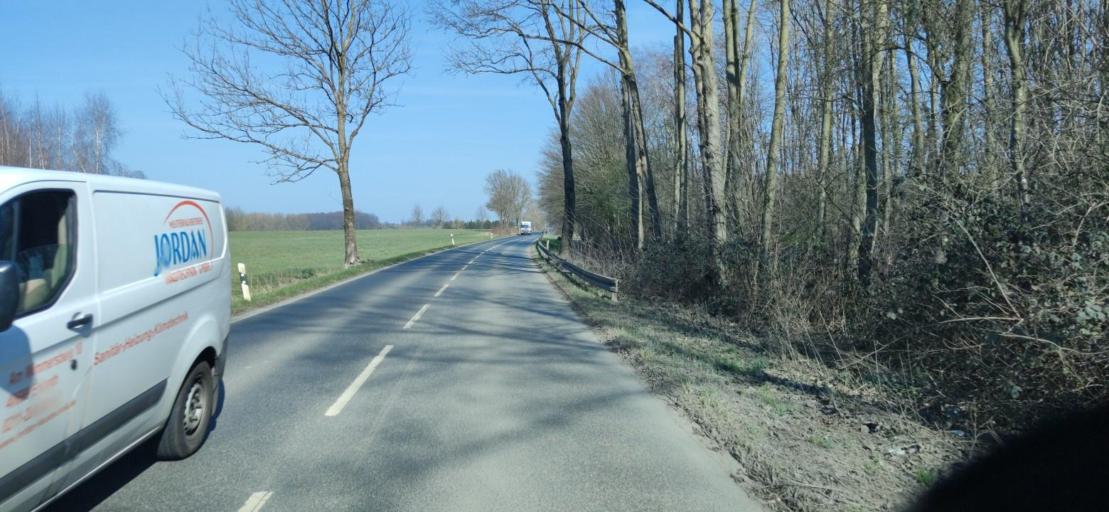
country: DE
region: North Rhine-Westphalia
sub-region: Regierungsbezirk Dusseldorf
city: Erkrath
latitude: 51.2452
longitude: 6.8939
